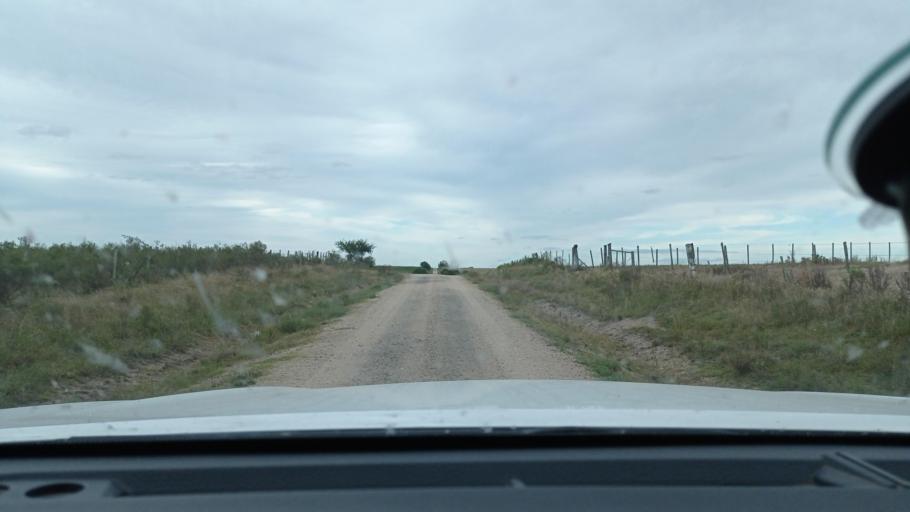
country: UY
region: Florida
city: Casupa
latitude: -34.1375
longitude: -55.7838
